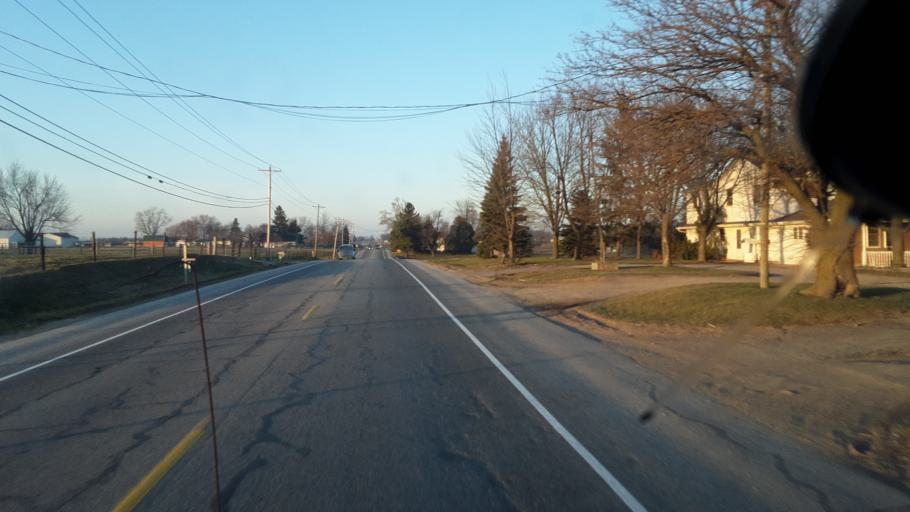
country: US
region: Indiana
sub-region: Allen County
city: Harlan
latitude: 41.2065
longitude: -84.9417
